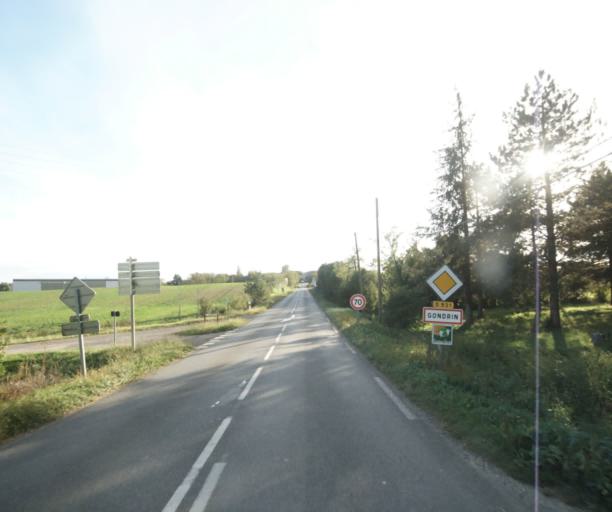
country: FR
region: Midi-Pyrenees
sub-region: Departement du Gers
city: Gondrin
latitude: 43.8916
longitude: 0.2422
